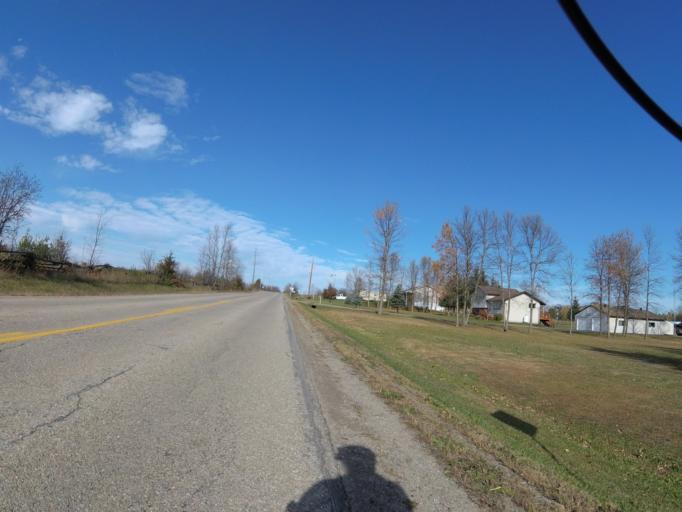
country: CA
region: Ontario
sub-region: Lanark County
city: Smiths Falls
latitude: 44.8337
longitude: -75.9361
